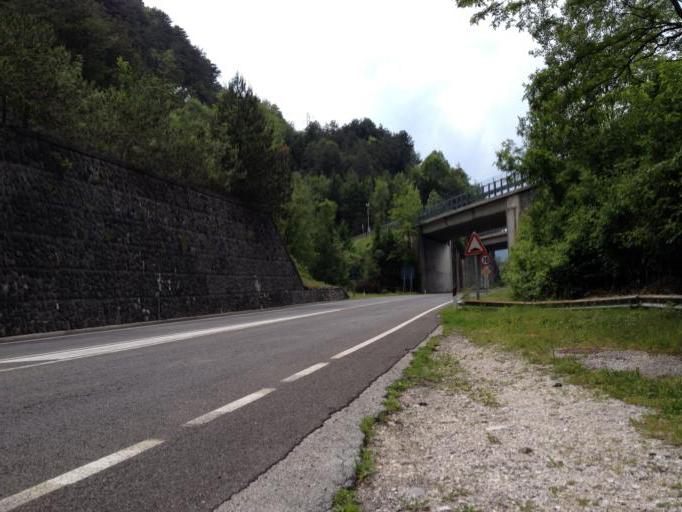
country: IT
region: Friuli Venezia Giulia
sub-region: Provincia di Udine
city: Moggio di Sotto
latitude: 46.3960
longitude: 13.2029
